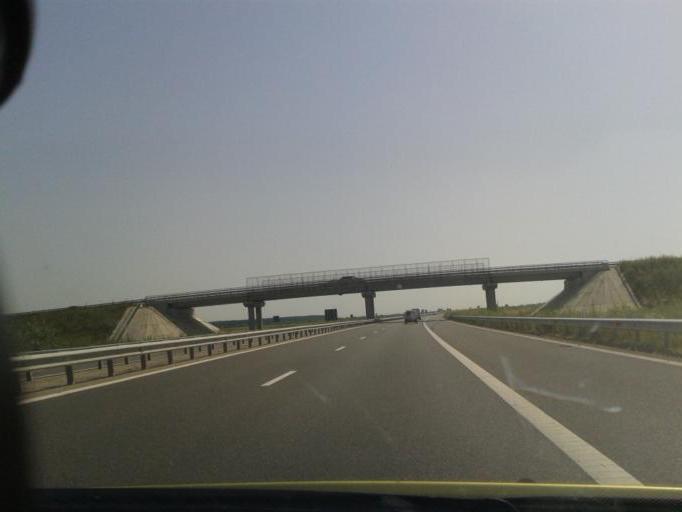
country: RO
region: Prahova
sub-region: Comuna Berceni
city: Corlatesti
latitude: 44.8868
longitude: 26.0955
